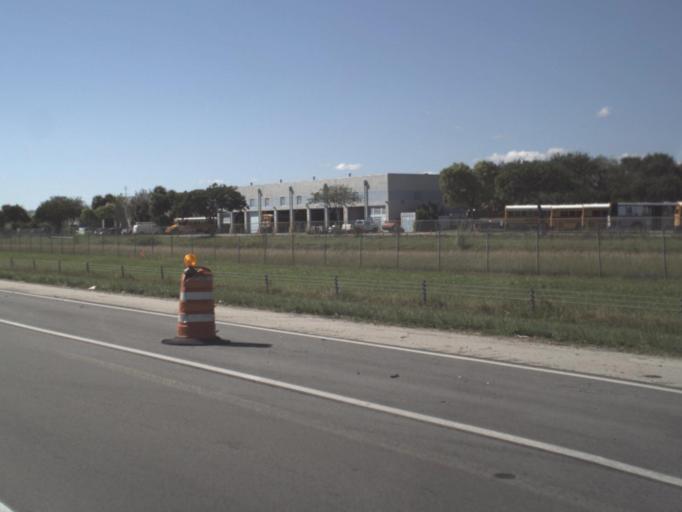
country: US
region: Florida
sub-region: Miami-Dade County
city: Richmond Heights
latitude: 25.6224
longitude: -80.3791
